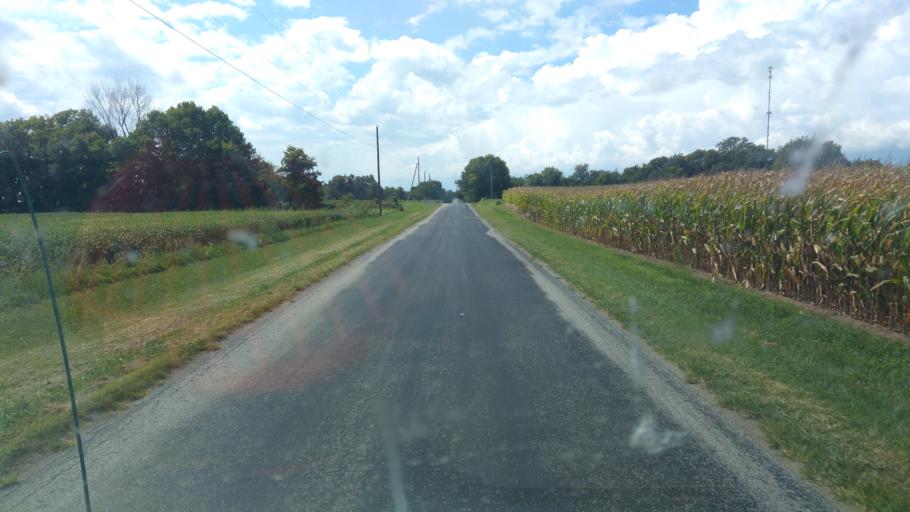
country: US
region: Ohio
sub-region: Union County
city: Richwood
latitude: 40.6001
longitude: -83.3830
